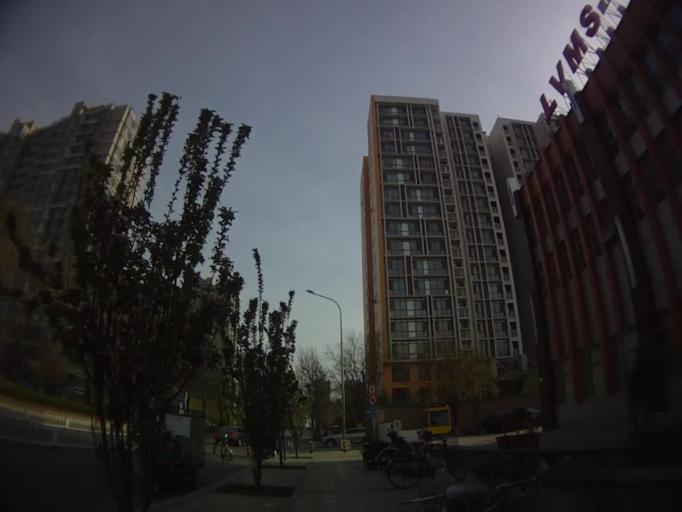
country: CN
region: Beijing
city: Longtan
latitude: 39.8952
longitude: 116.4441
